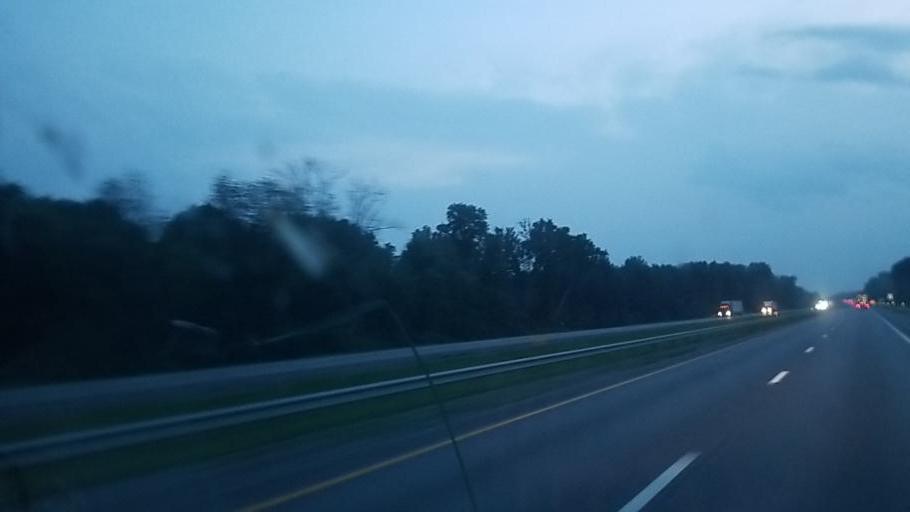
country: US
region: New York
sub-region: Onondaga County
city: Minoa
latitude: 43.0929
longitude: -75.9655
